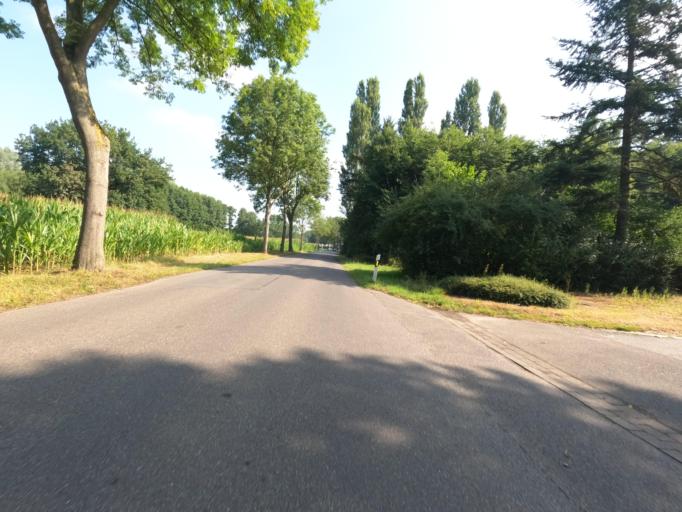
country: DE
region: North Rhine-Westphalia
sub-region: Regierungsbezirk Koln
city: Heinsberg
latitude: 51.0792
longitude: 6.0815
